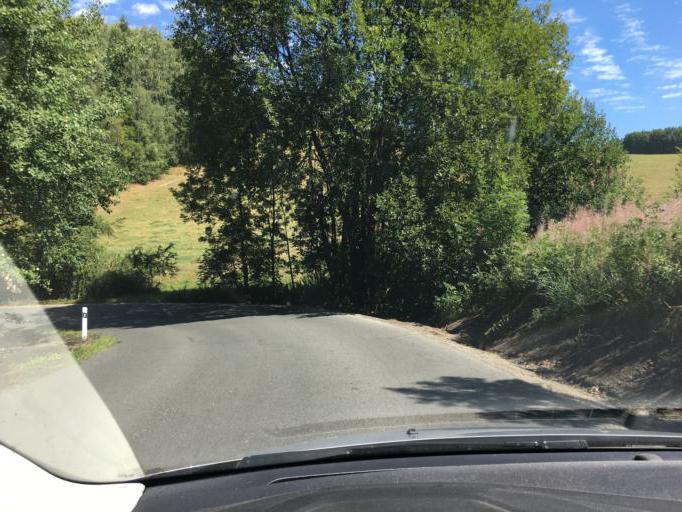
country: CZ
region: Liberecky
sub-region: Okres Semily
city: Vysoke nad Jizerou
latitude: 50.7029
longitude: 15.3676
